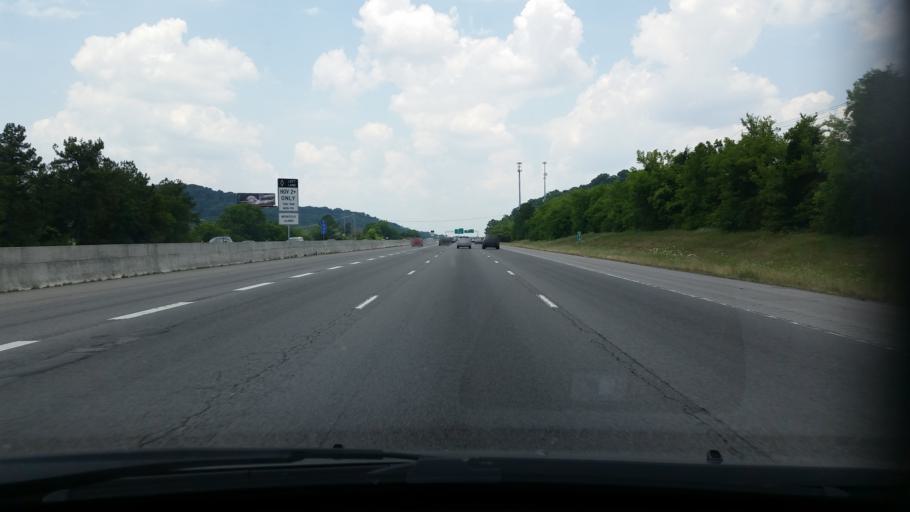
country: US
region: Tennessee
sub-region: Williamson County
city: Brentwood
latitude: 36.0299
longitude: -86.7837
